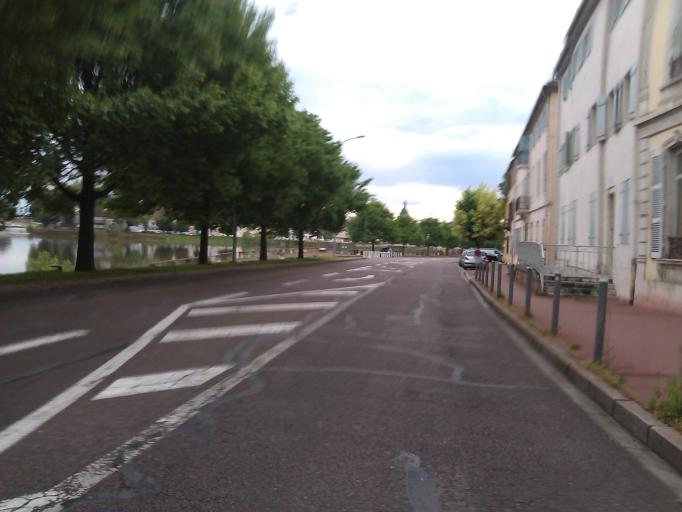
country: FR
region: Bourgogne
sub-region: Departement de Saone-et-Loire
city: Chalon-sur-Saone
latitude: 46.7833
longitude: 4.8640
